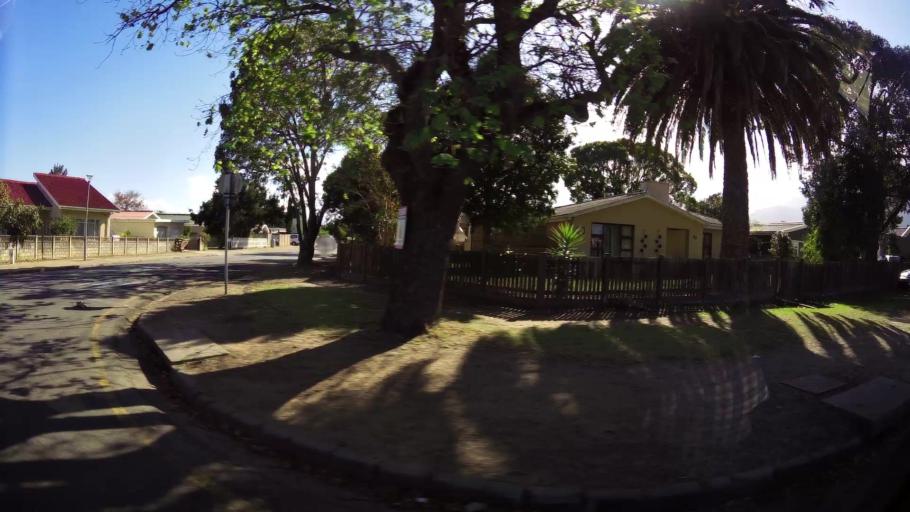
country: ZA
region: Western Cape
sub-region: Eden District Municipality
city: George
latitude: -33.9685
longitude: 22.4535
